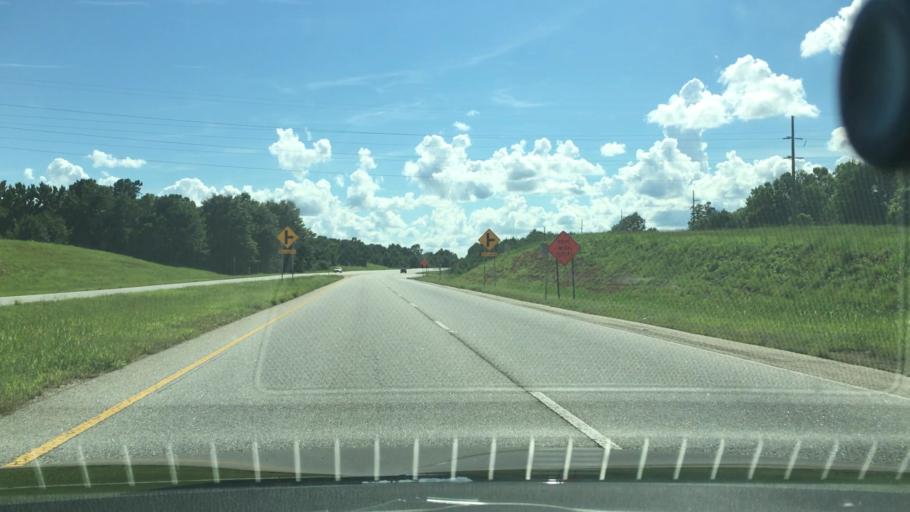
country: US
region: Georgia
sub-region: Spalding County
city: East Griffin
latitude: 33.2361
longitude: -84.2161
